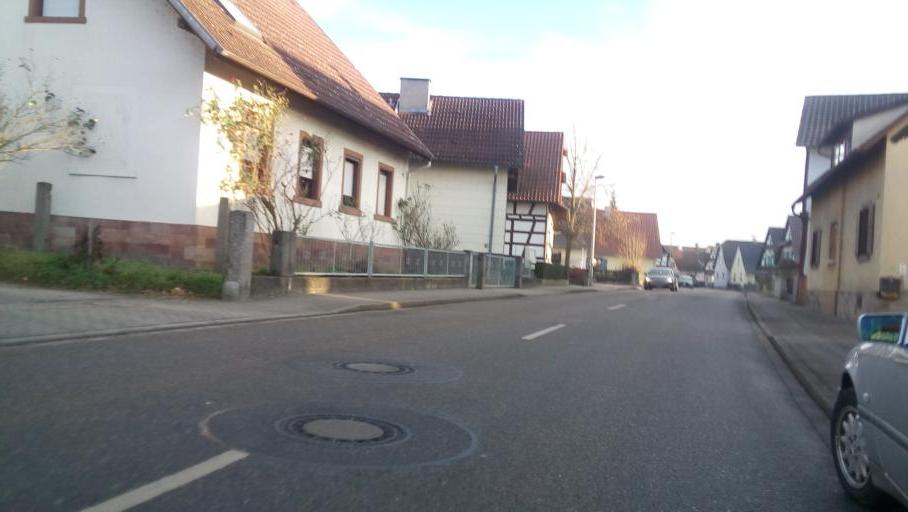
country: DE
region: Baden-Wuerttemberg
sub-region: Freiburg Region
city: Rheinau
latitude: 48.6838
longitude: 7.9794
